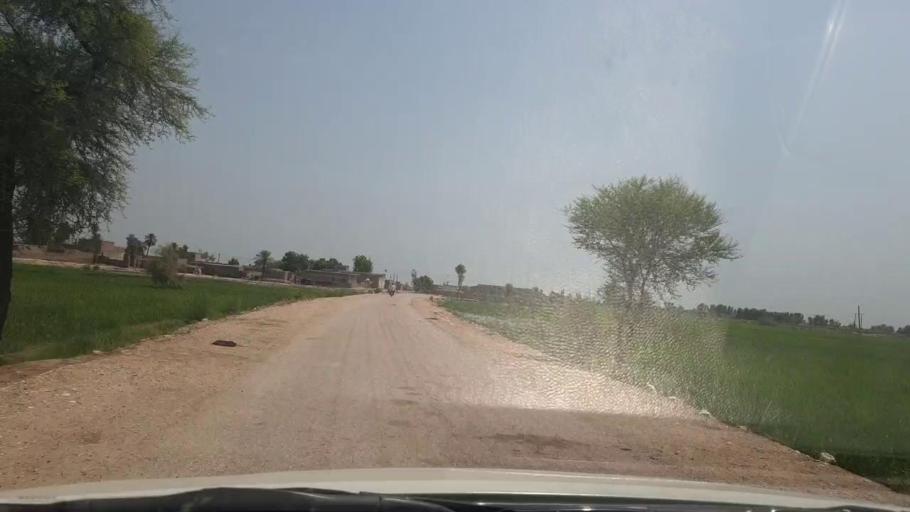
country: PK
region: Sindh
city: Rustam jo Goth
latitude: 28.0269
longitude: 68.7993
